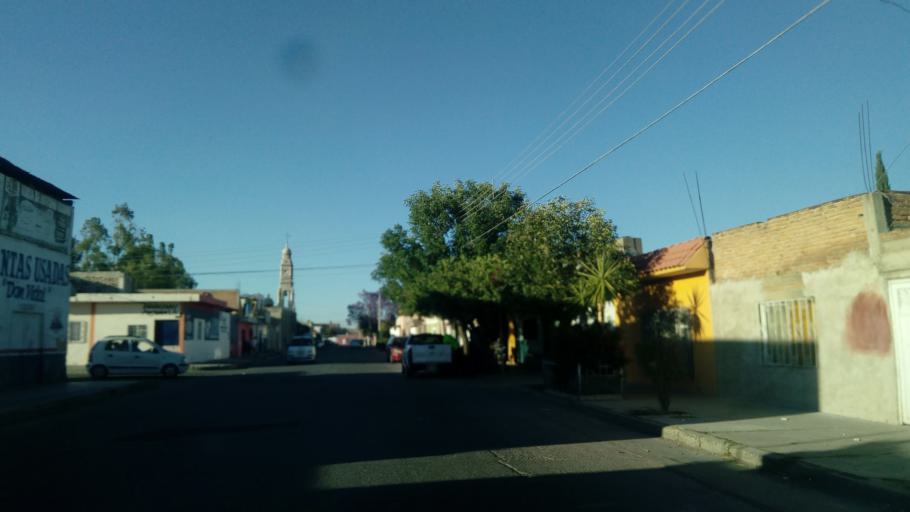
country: MX
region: Durango
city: Victoria de Durango
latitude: 23.9996
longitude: -104.6749
